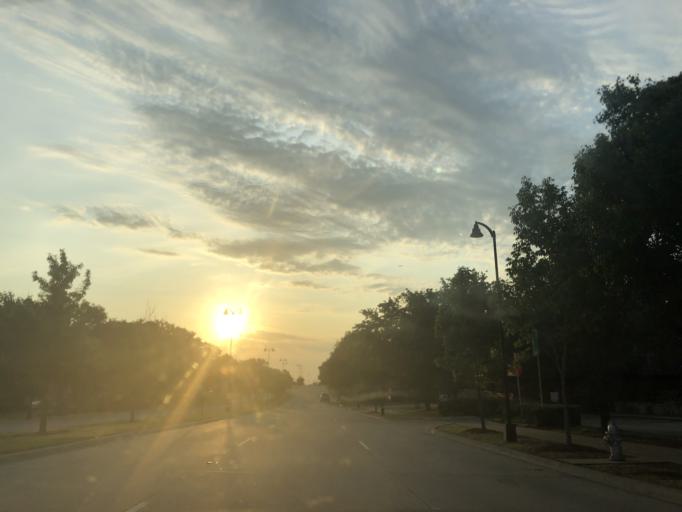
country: US
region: Texas
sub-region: Tarrant County
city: Arlington
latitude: 32.7645
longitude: -97.0927
